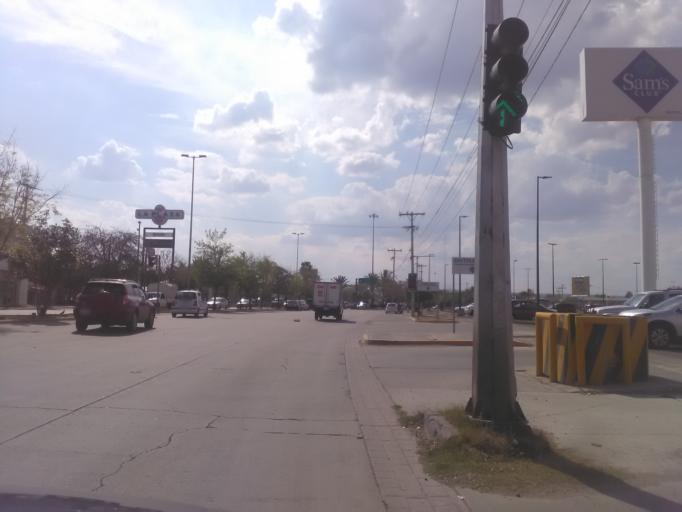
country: MX
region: Durango
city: Victoria de Durango
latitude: 24.0031
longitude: -104.6514
